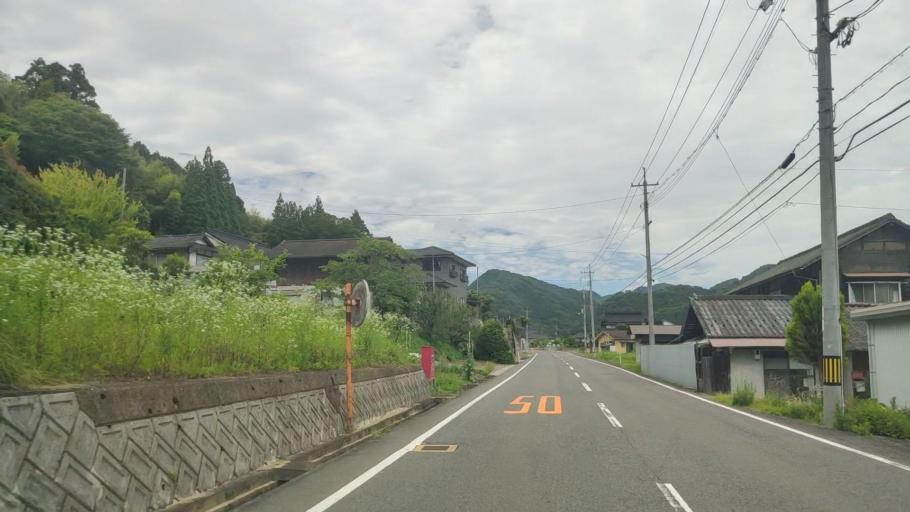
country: JP
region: Hyogo
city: Yamazakicho-nakabirose
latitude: 35.0961
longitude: 134.2965
